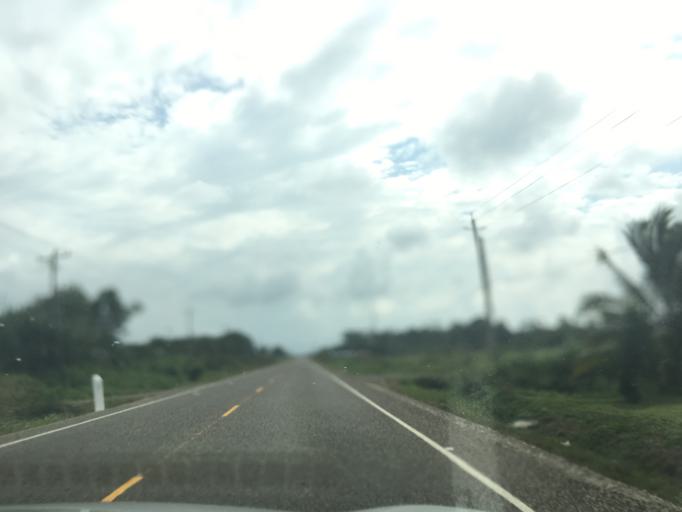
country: BZ
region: Stann Creek
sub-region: Dangriga
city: Dangriga
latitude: 16.9919
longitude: -88.2998
